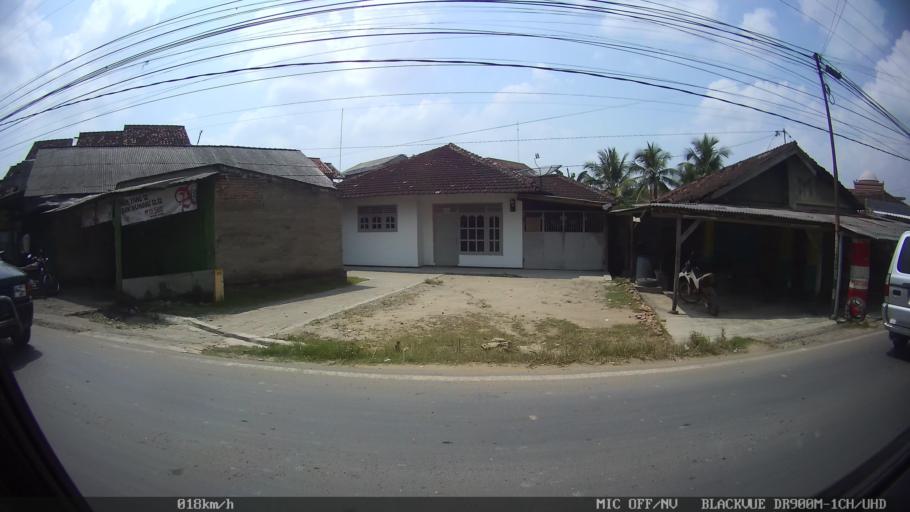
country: ID
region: Lampung
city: Pringsewu
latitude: -5.3640
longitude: 104.9739
